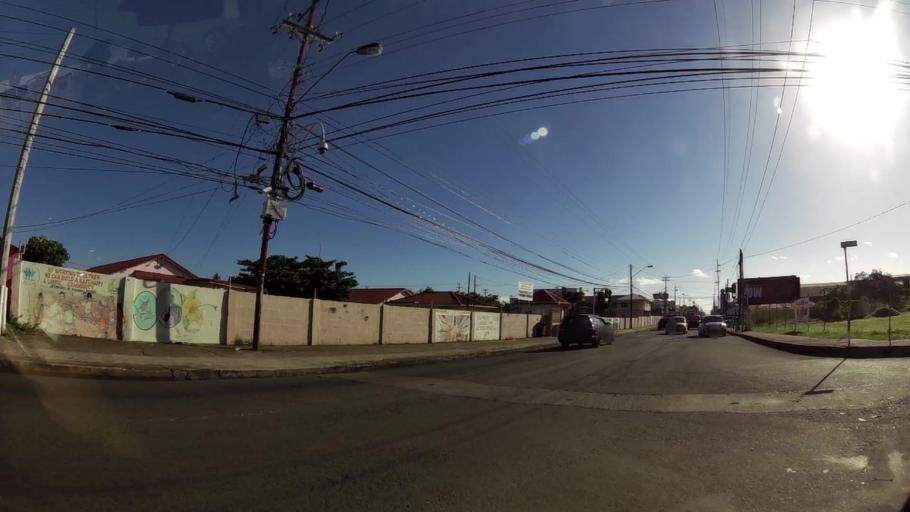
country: TT
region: Tobago
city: Scarborough
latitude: 11.1573
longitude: -60.8182
